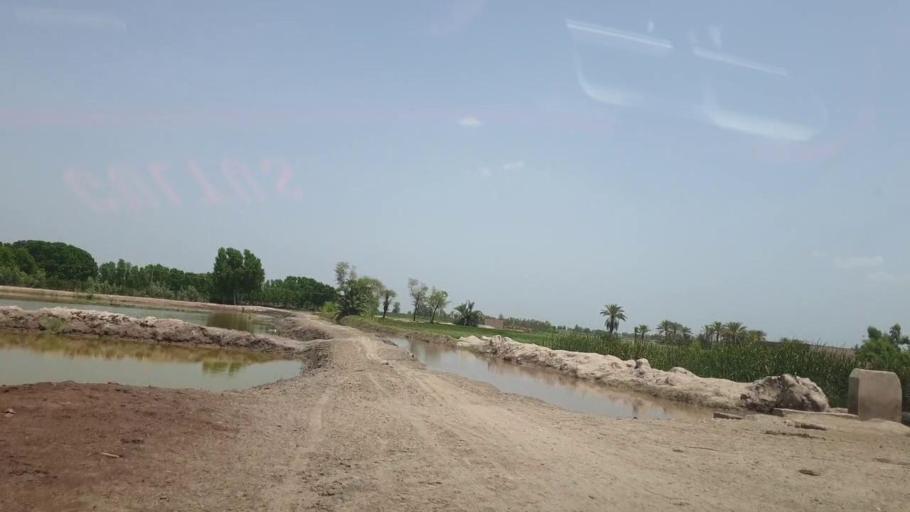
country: PK
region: Sindh
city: Daulatpur
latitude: 26.4880
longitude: 68.1408
